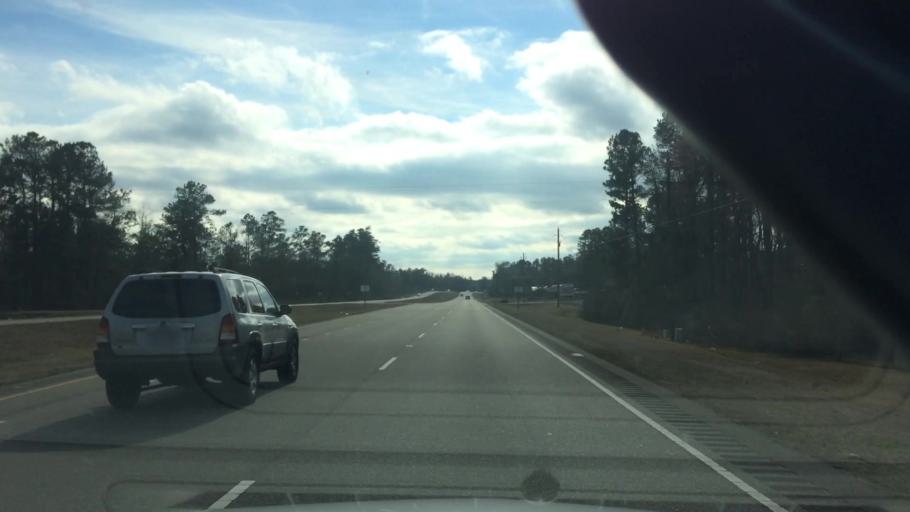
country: US
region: North Carolina
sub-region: Brunswick County
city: Bolivia
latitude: 34.1243
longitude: -78.1050
